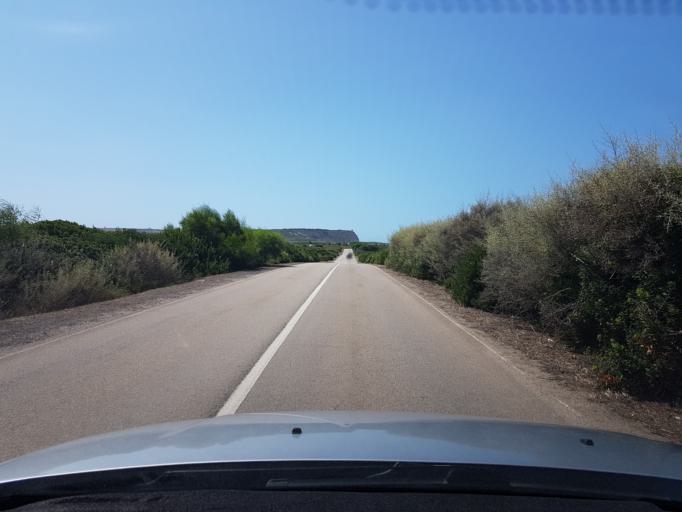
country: IT
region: Sardinia
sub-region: Provincia di Oristano
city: Riola Sardo
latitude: 40.0398
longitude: 8.4104
